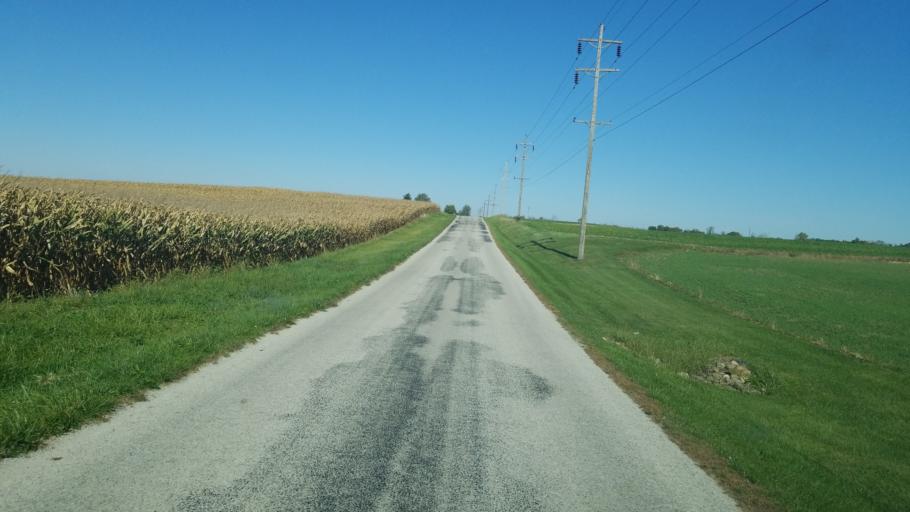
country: US
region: Ohio
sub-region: Huron County
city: Plymouth
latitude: 40.9749
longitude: -82.6958
